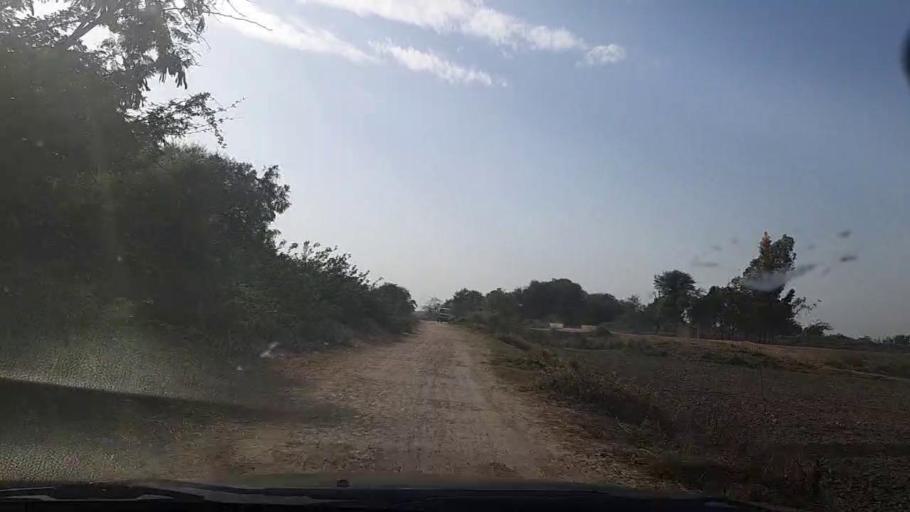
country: PK
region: Sindh
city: Mirpur Batoro
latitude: 24.5530
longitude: 68.1734
